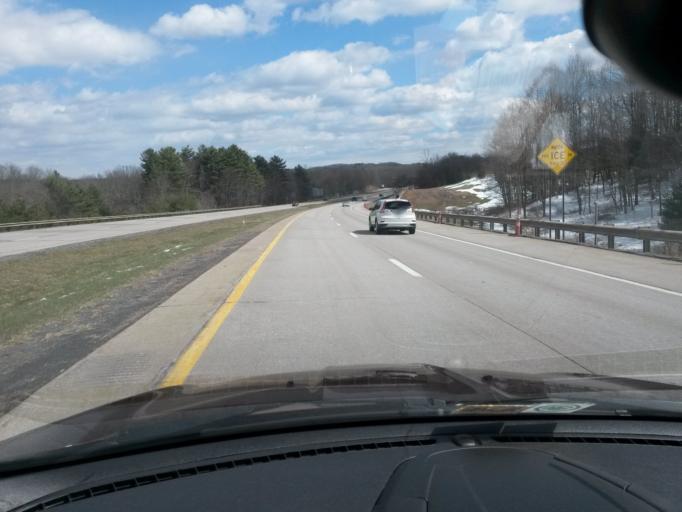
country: US
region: West Virginia
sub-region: Raleigh County
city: Daniels
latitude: 37.7727
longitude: -81.0500
